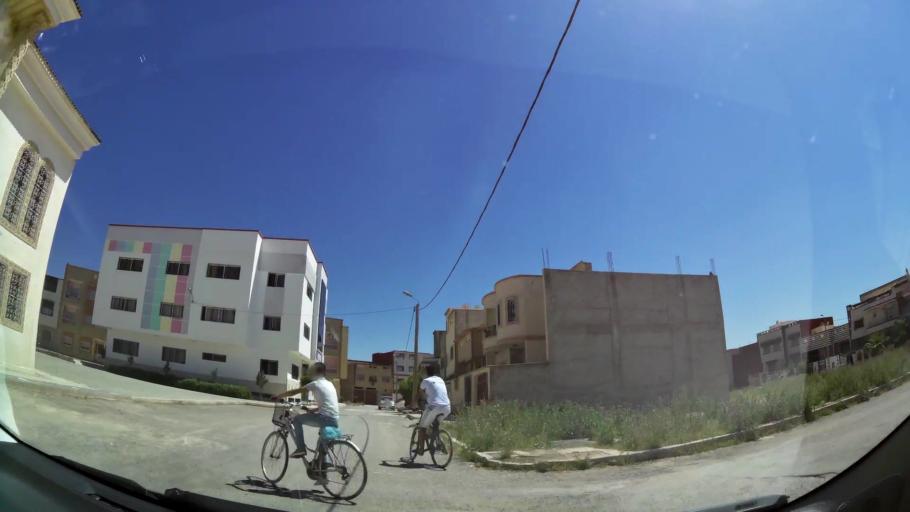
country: MA
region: Oriental
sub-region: Oujda-Angad
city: Oujda
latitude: 34.6709
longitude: -1.8686
